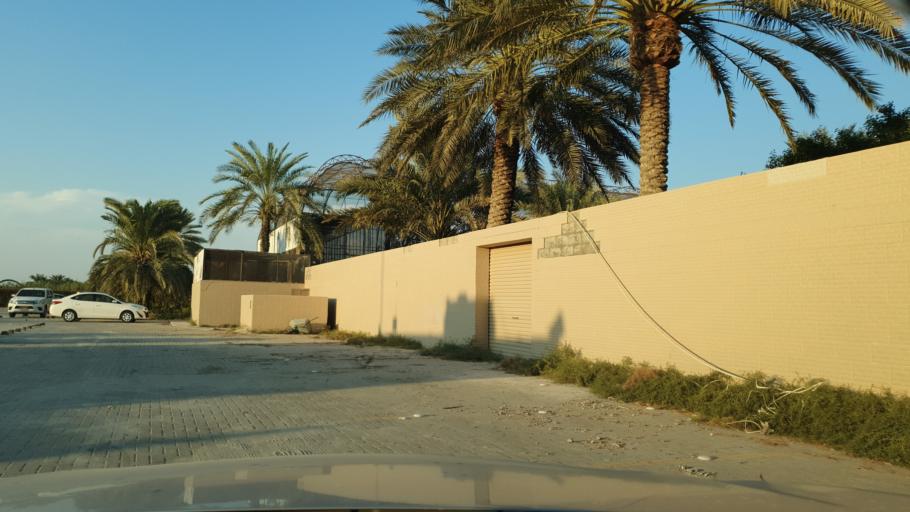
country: BH
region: Central Governorate
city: Dar Kulayb
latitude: 26.0159
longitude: 50.4946
